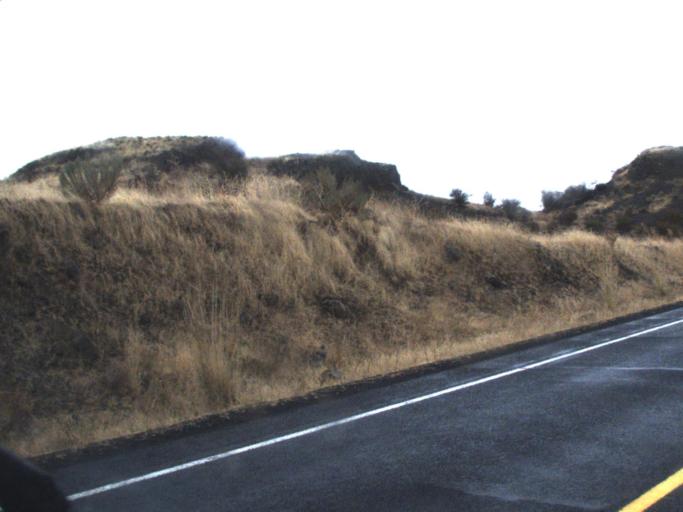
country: US
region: Washington
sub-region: Spokane County
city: Medical Lake
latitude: 47.2886
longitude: -117.9660
